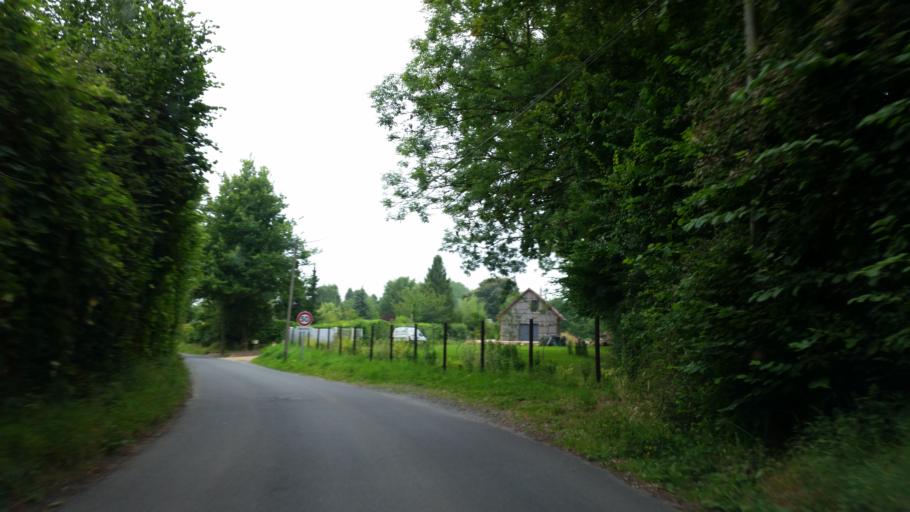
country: FR
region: Lower Normandy
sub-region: Departement du Calvados
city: Equemauville
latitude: 49.3895
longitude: 0.2369
